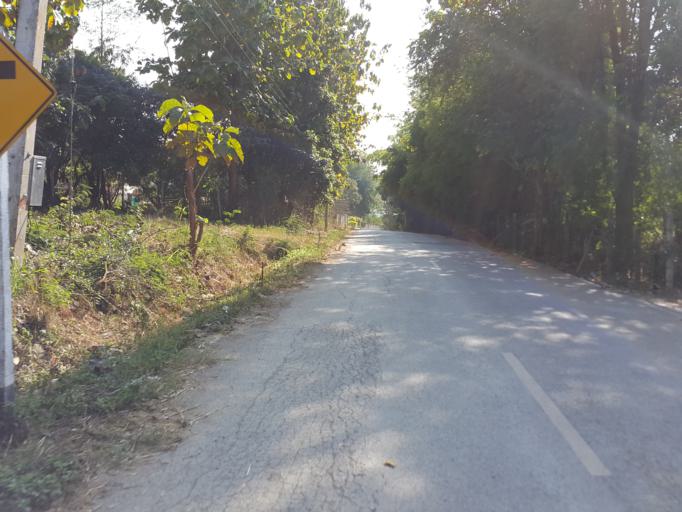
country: TH
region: Chiang Mai
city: Mae On
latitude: 18.8286
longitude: 99.2329
